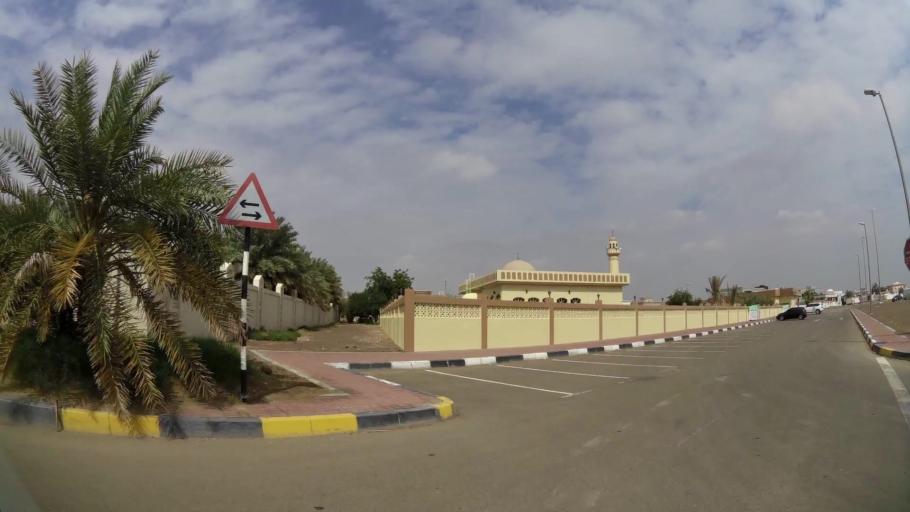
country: AE
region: Abu Dhabi
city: Al Ain
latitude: 24.1983
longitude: 55.8008
